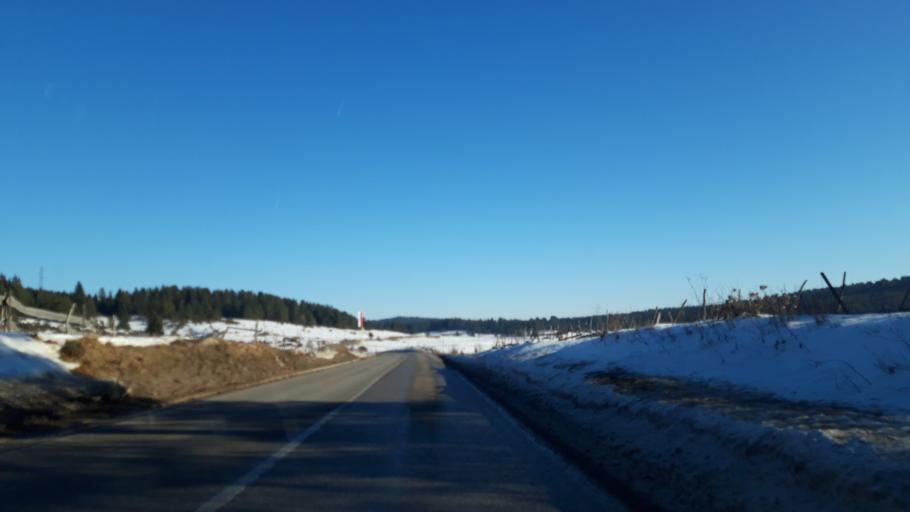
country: BA
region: Republika Srpska
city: Sokolac
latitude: 43.9229
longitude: 18.6775
